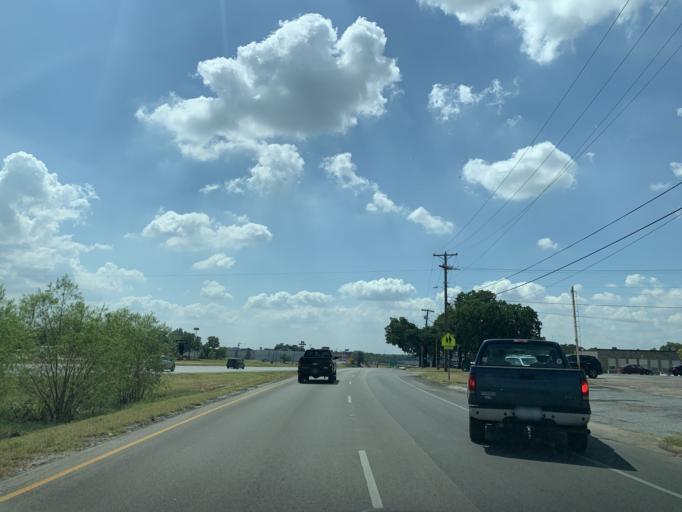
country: US
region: Texas
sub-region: Tarrant County
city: Azle
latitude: 32.8972
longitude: -97.5429
